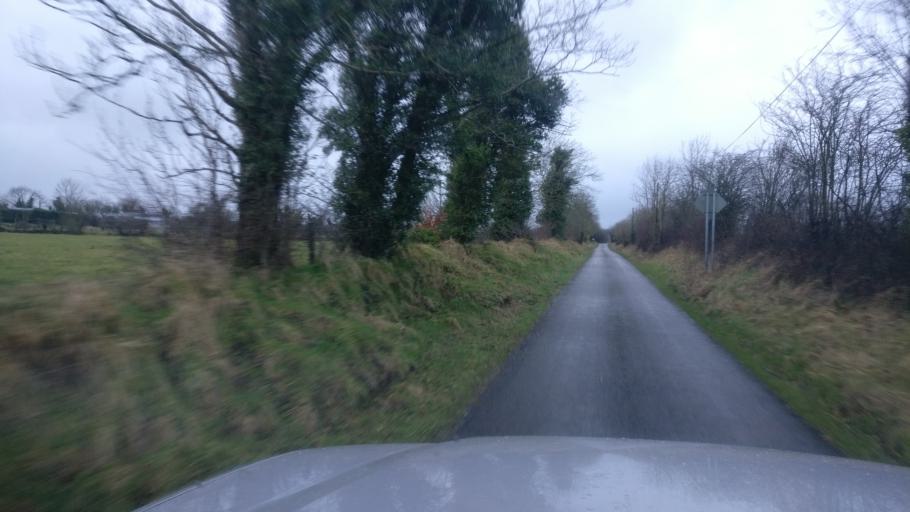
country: IE
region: Connaught
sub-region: County Galway
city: Ballinasloe
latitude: 53.2760
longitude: -8.3363
